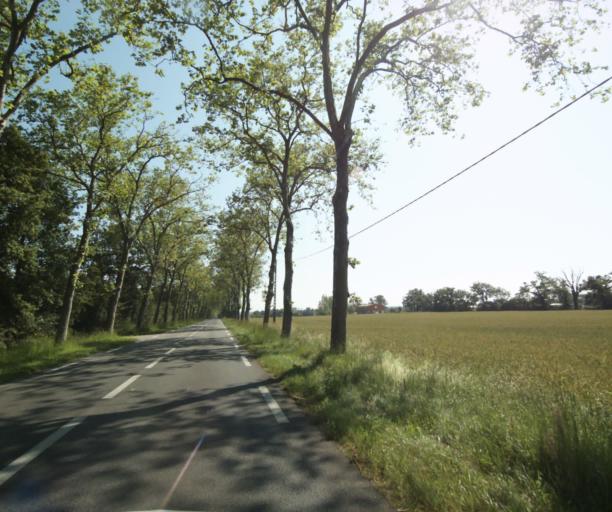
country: FR
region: Midi-Pyrenees
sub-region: Departement du Tarn-et-Garonne
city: Montbeton
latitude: 43.9856
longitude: 1.3019
